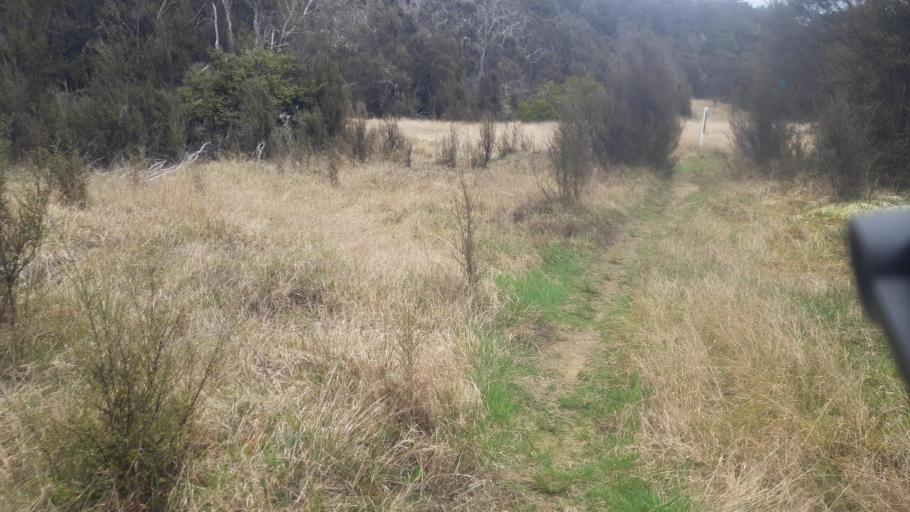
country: NZ
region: Tasman
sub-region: Tasman District
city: Wakefield
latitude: -41.7791
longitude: 172.8154
